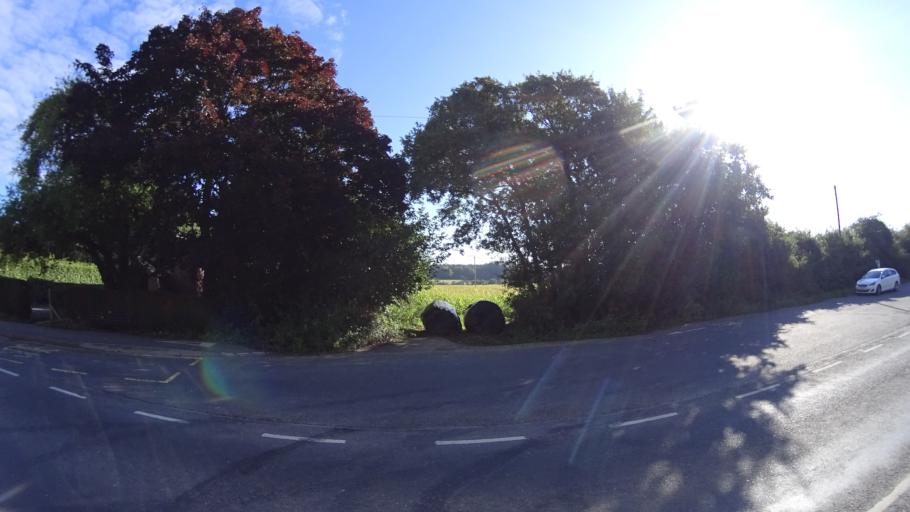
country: GB
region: England
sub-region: Hampshire
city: Romsey
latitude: 51.0193
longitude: -1.5050
